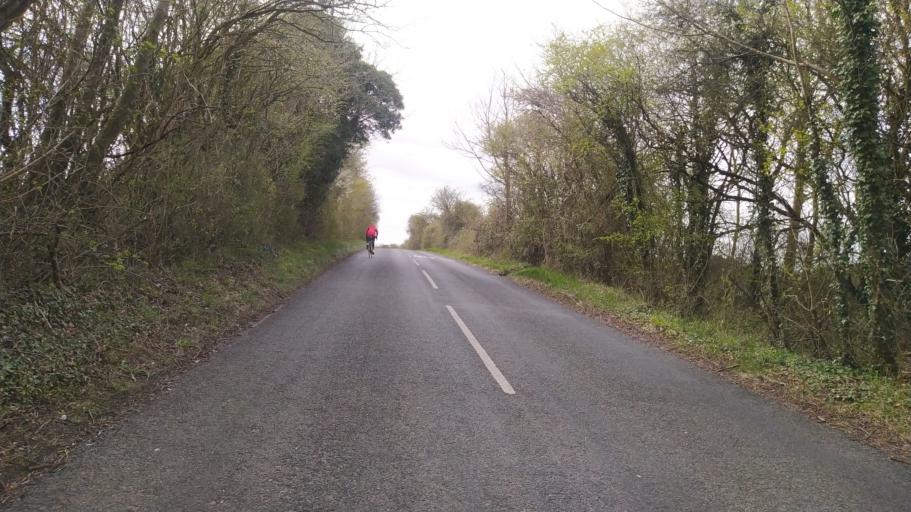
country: GB
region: England
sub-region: Hampshire
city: Bishops Waltham
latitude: 50.9888
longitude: -1.2048
